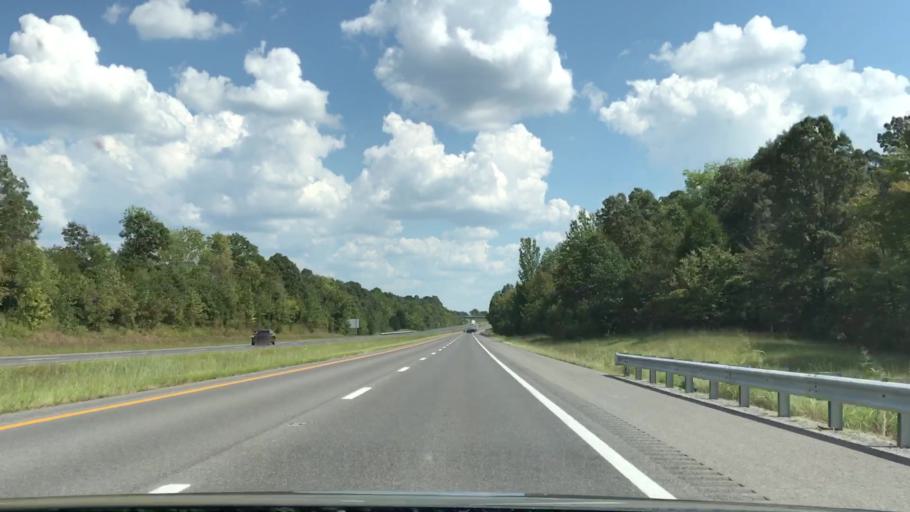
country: US
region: Kentucky
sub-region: Lyon County
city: Eddyville
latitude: 37.1092
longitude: -88.0109
